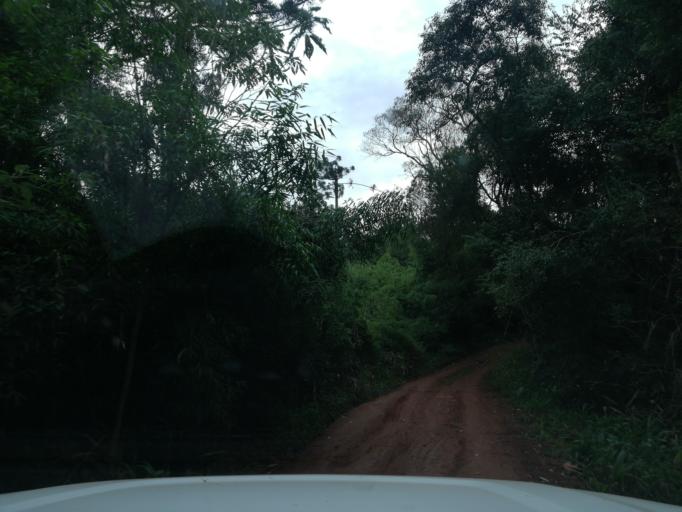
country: AR
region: Misiones
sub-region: Departamento de San Pedro
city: San Pedro
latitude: -26.6322
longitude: -54.0960
